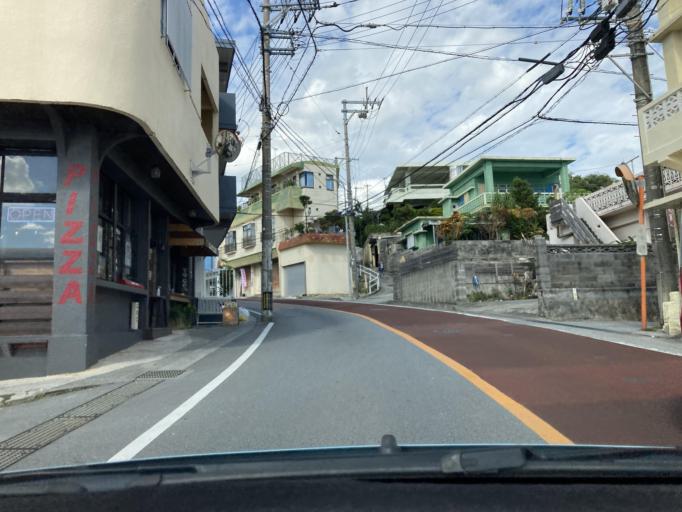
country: JP
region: Okinawa
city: Chatan
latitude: 26.3156
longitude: 127.7724
